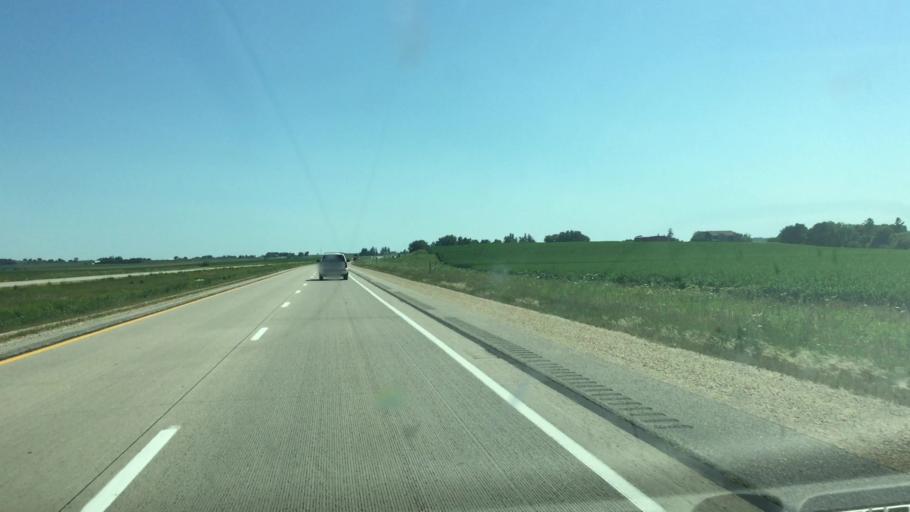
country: US
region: Iowa
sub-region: Jones County
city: Monticello
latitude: 42.1926
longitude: -91.2160
